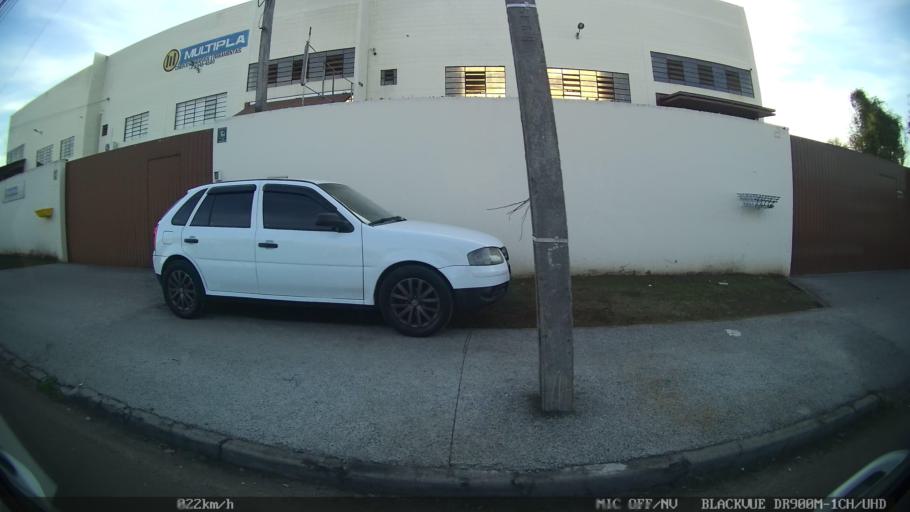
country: BR
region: Parana
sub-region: Pinhais
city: Pinhais
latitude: -25.4402
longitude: -49.1753
